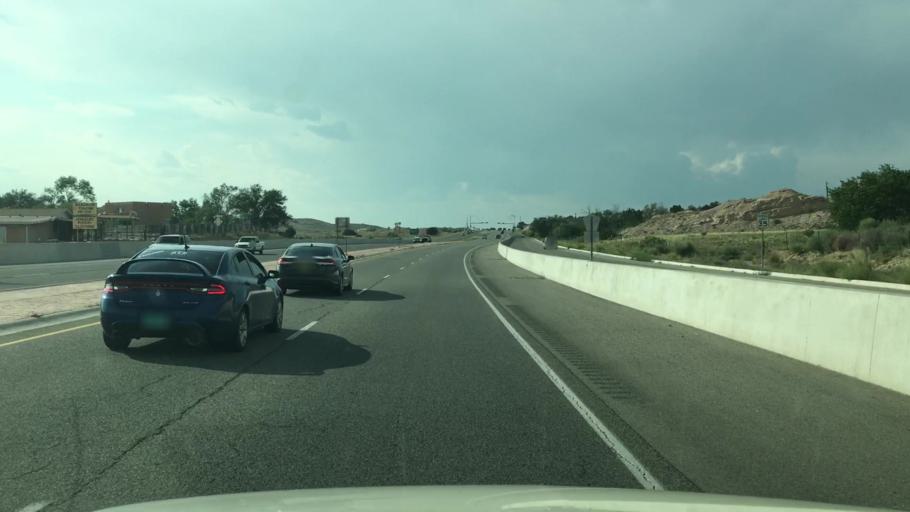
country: US
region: New Mexico
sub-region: Santa Fe County
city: El Valle de Arroyo Seco
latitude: 35.9704
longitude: -106.0391
